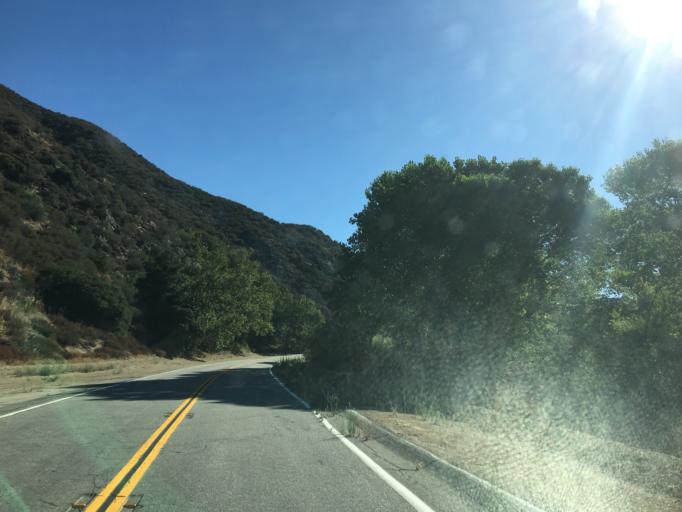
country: US
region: California
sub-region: Los Angeles County
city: Green Valley
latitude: 34.6439
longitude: -118.5197
